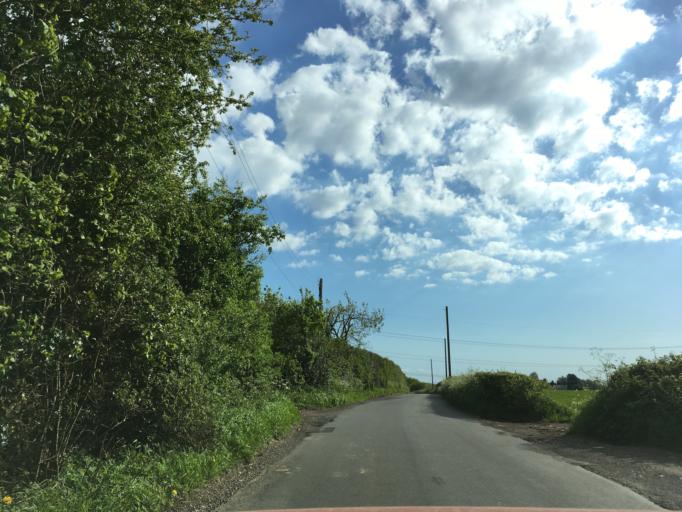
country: GB
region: Wales
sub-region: Newport
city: Marshfield
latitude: 51.5636
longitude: -3.0653
